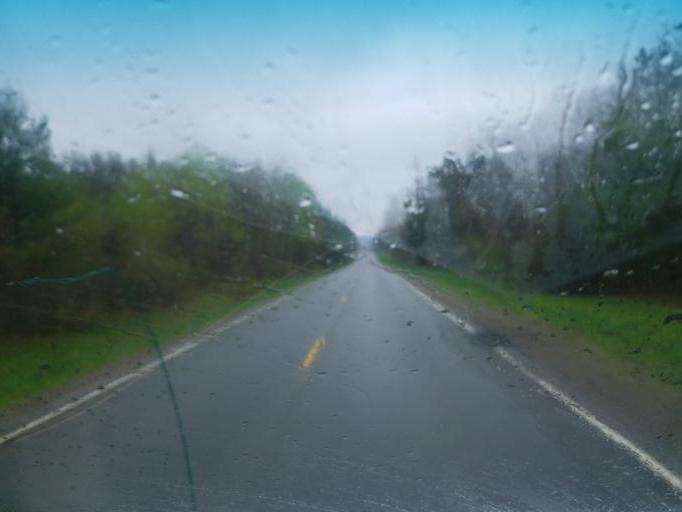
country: US
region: New York
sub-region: Allegany County
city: Friendship
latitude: 42.1829
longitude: -78.0816
